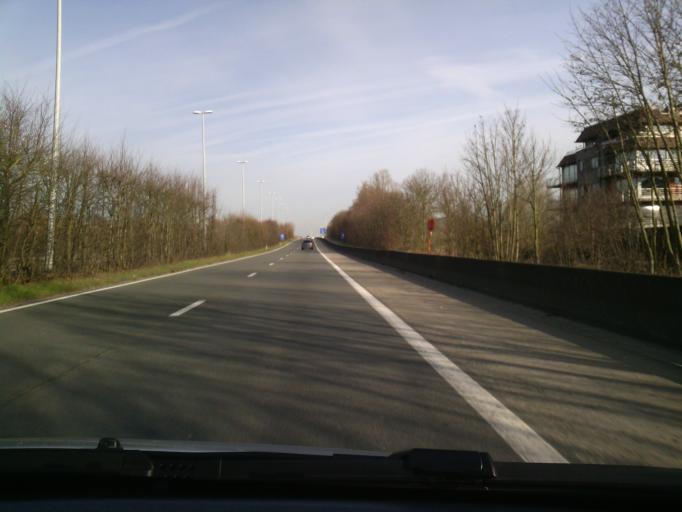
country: FR
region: Nord-Pas-de-Calais
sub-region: Departement du Nord
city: Halluin
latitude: 50.7911
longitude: 3.1385
